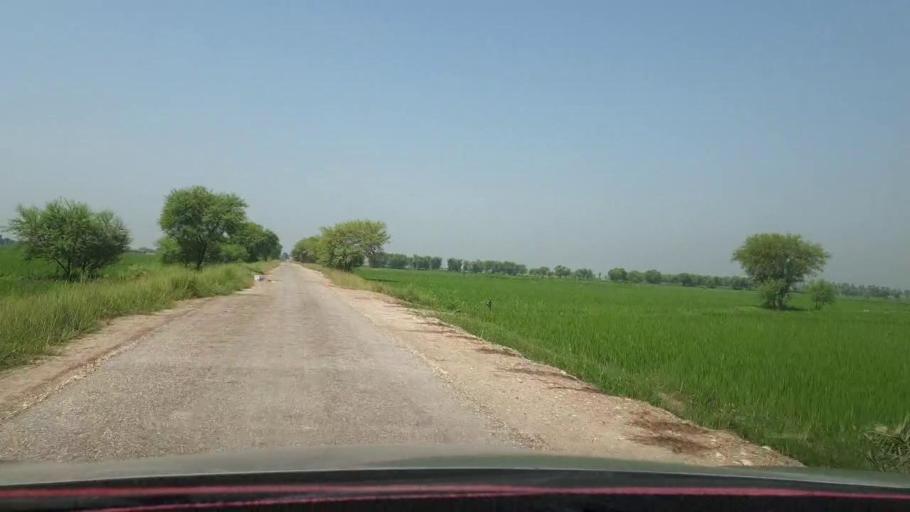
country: PK
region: Sindh
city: Kambar
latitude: 27.6113
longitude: 67.8789
